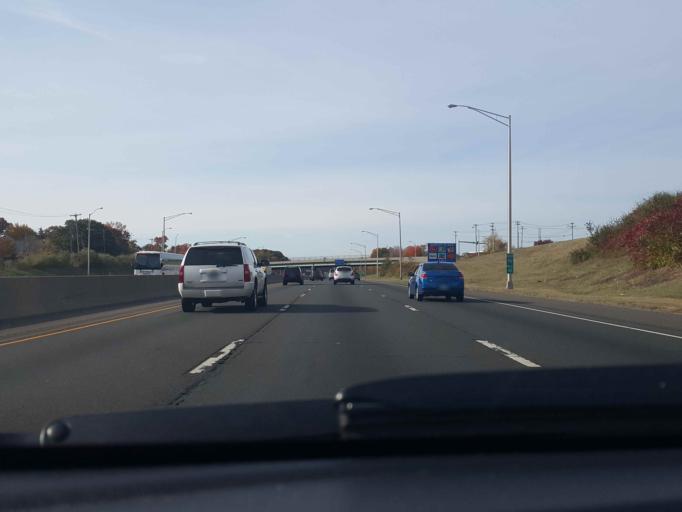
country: US
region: Connecticut
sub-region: New Haven County
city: Woodmont
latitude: 41.2555
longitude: -72.9968
